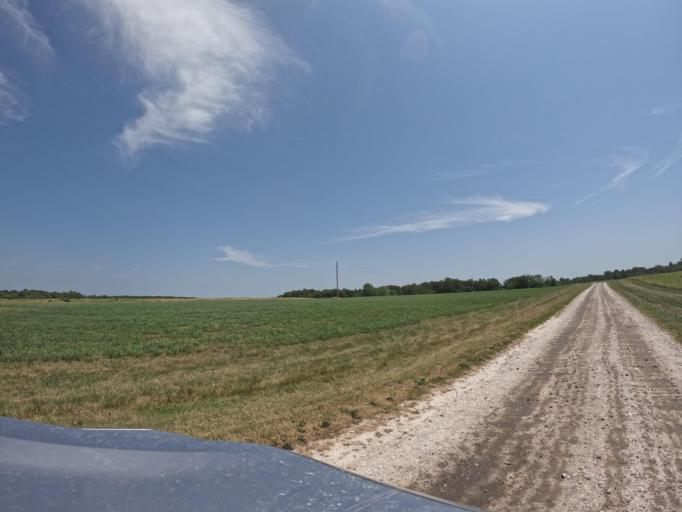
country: US
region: Iowa
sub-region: Henry County
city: Mount Pleasant
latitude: 40.9418
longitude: -91.5882
